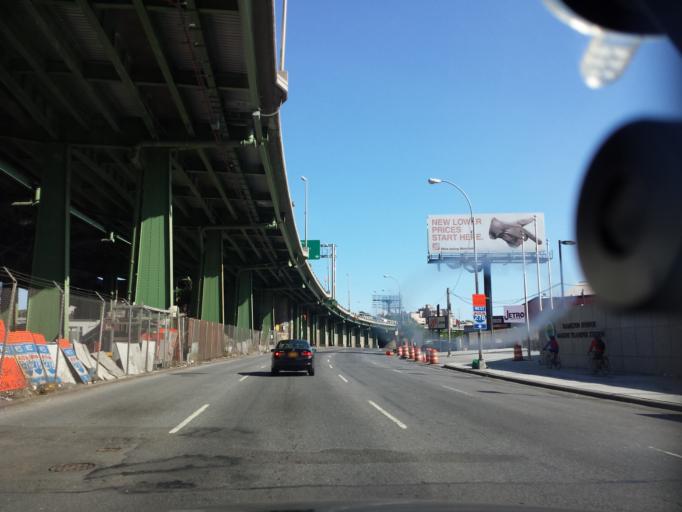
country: US
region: New York
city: New York City
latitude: 40.6684
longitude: -73.9968
